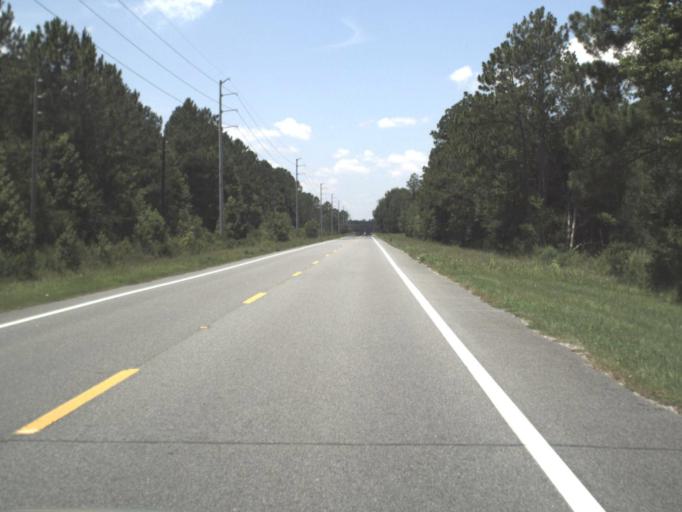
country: US
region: Florida
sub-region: Bradford County
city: Starke
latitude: 29.9553
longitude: -82.0611
